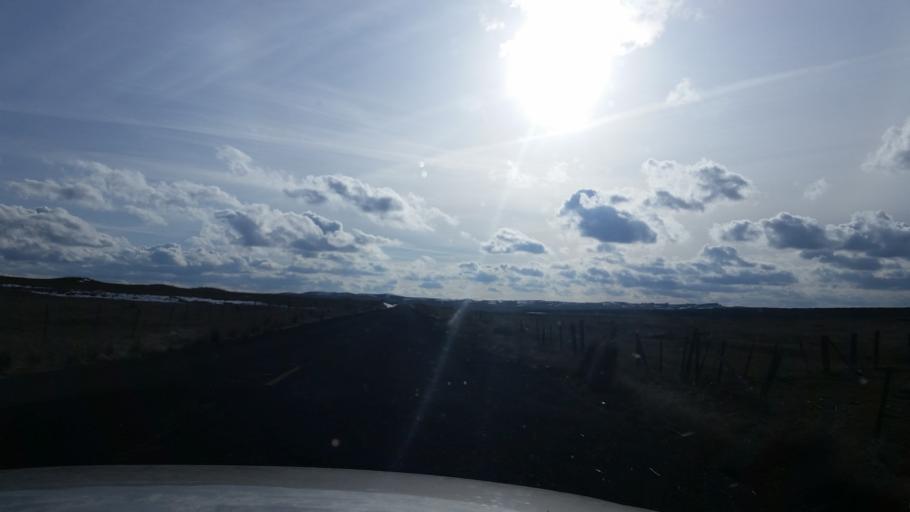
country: US
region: Washington
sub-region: Spokane County
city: Cheney
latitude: 47.2748
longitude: -117.6544
